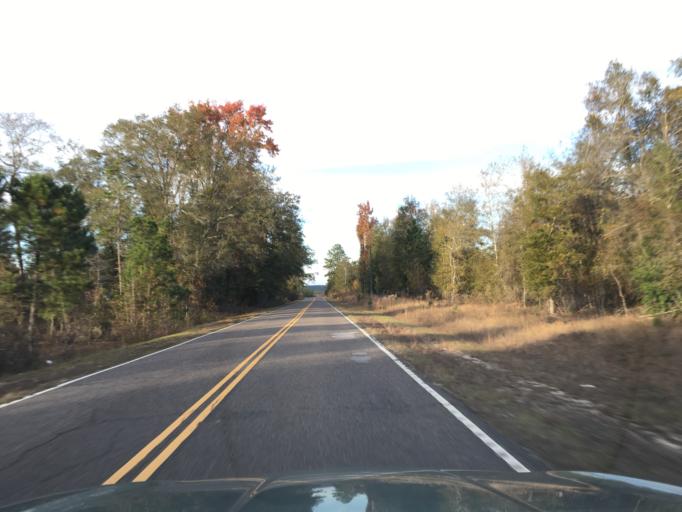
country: US
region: South Carolina
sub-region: Lexington County
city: Red Bank
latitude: 33.7082
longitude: -81.3559
